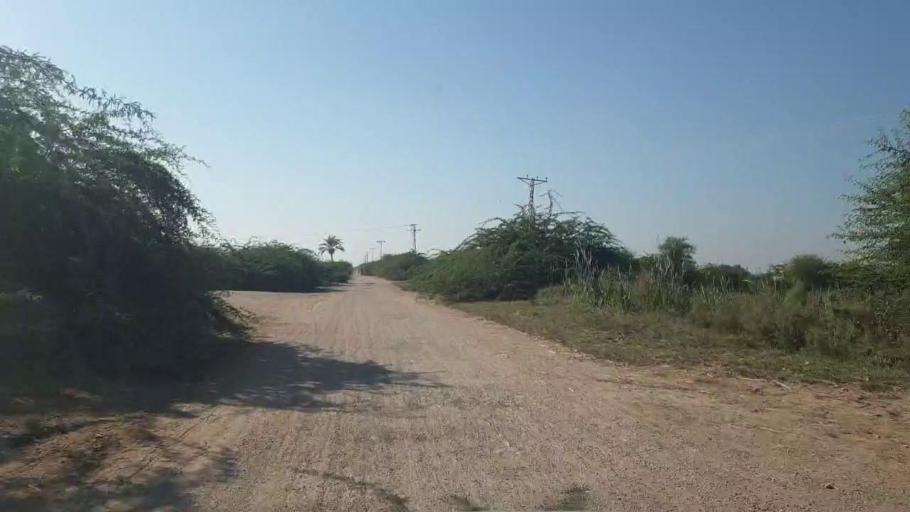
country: PK
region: Sindh
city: Rajo Khanani
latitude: 24.9527
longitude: 68.7948
